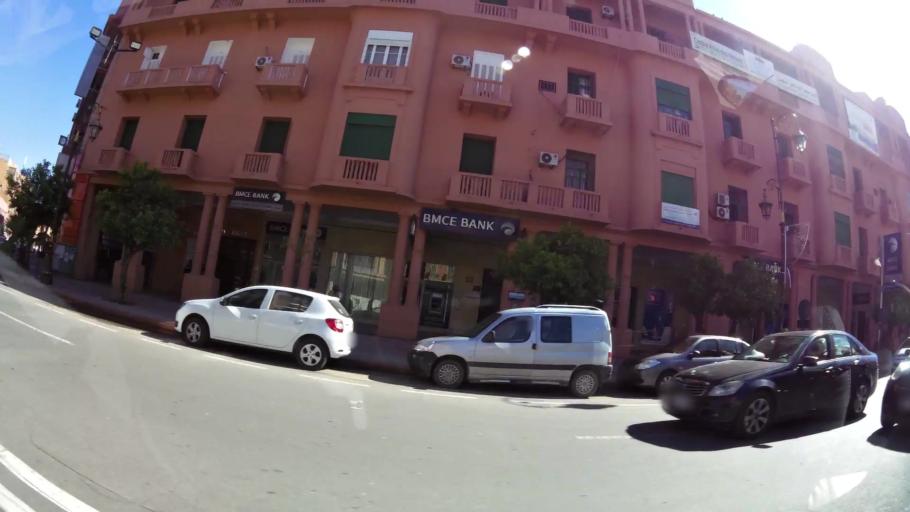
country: MA
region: Marrakech-Tensift-Al Haouz
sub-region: Marrakech
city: Marrakesh
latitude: 31.6368
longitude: -8.0159
